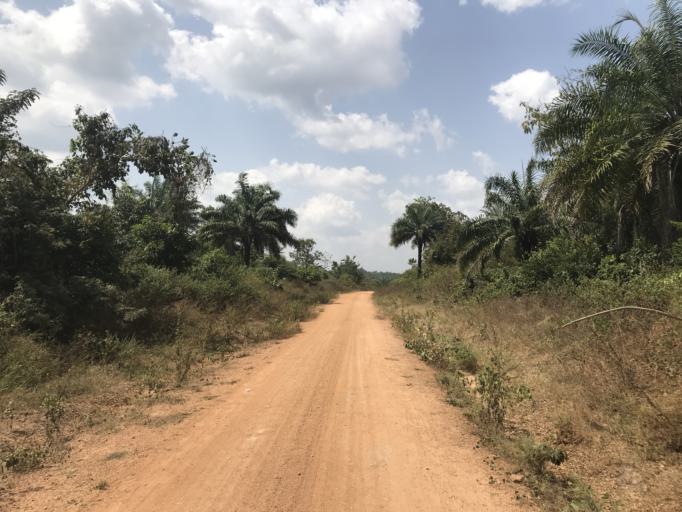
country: NG
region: Osun
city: Ifon
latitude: 7.9787
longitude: 4.5177
